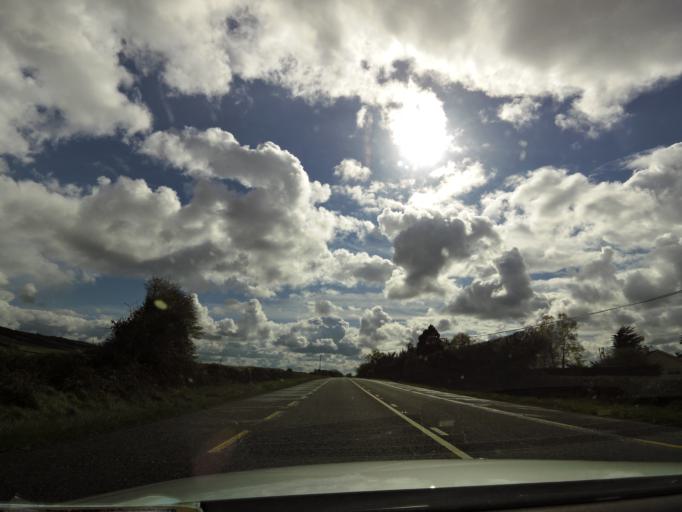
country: IE
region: Leinster
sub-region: Laois
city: Rathdowney
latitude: 52.8121
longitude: -7.4857
